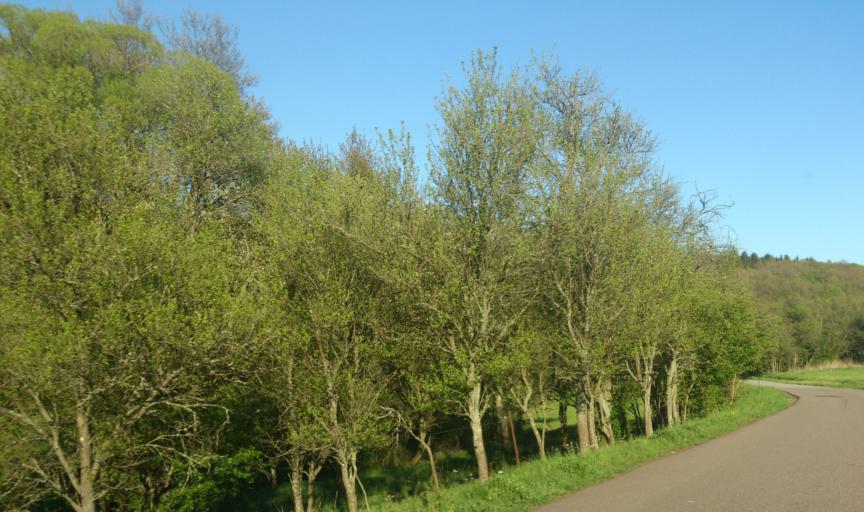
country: DE
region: Rheinland-Pfalz
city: Hahnweiler
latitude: 49.5450
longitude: 7.1999
